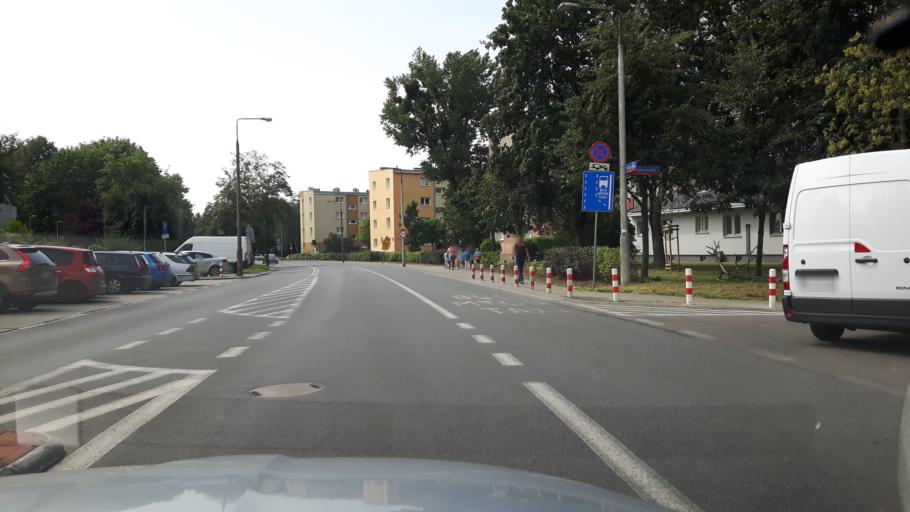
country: PL
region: Masovian Voivodeship
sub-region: Warszawa
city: Ochota
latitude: 52.2362
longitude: 20.9478
